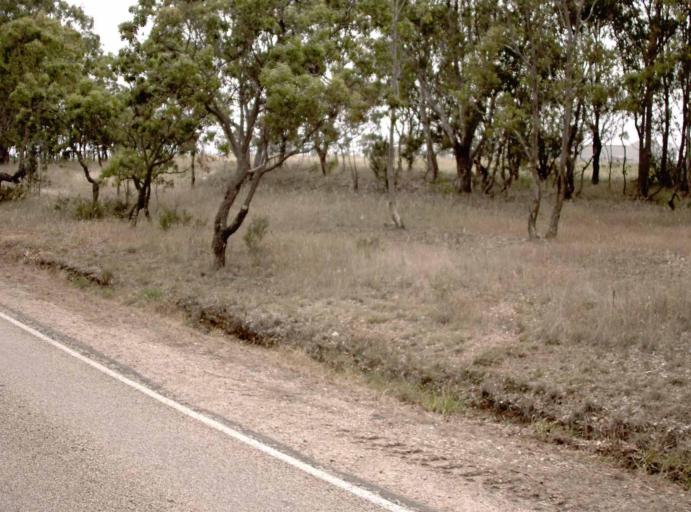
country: AU
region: Victoria
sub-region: Wellington
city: Sale
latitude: -37.9475
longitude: 147.0894
